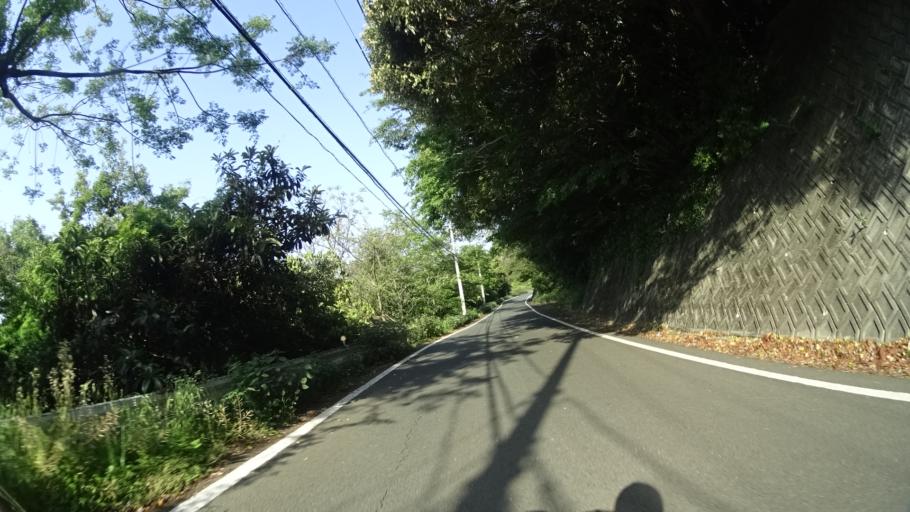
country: JP
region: Ehime
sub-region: Nishiuwa-gun
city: Ikata-cho
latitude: 33.3893
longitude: 132.0994
